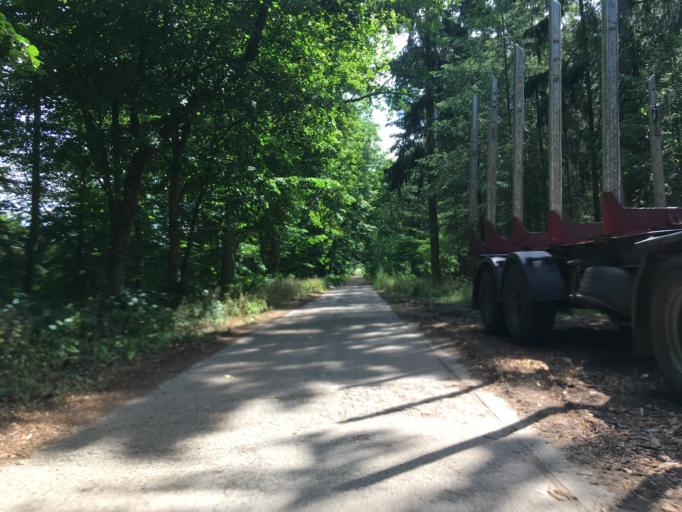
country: DE
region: Brandenburg
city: Passow
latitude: 53.2020
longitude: 14.1297
